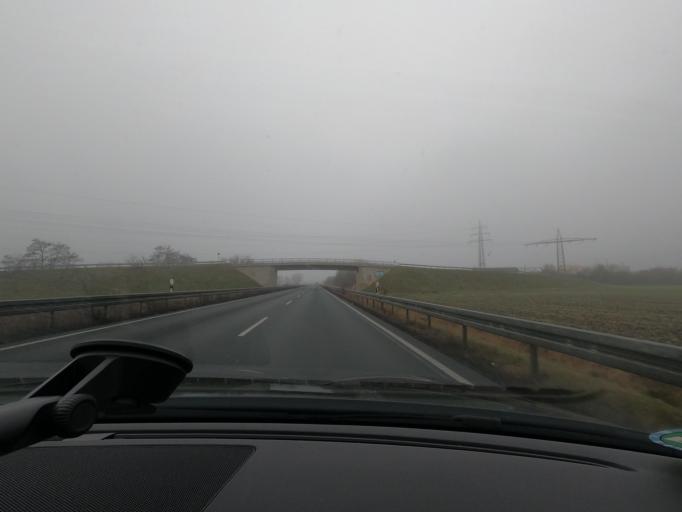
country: DE
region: North Rhine-Westphalia
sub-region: Regierungsbezirk Koln
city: Dueren
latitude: 50.7860
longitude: 6.5190
